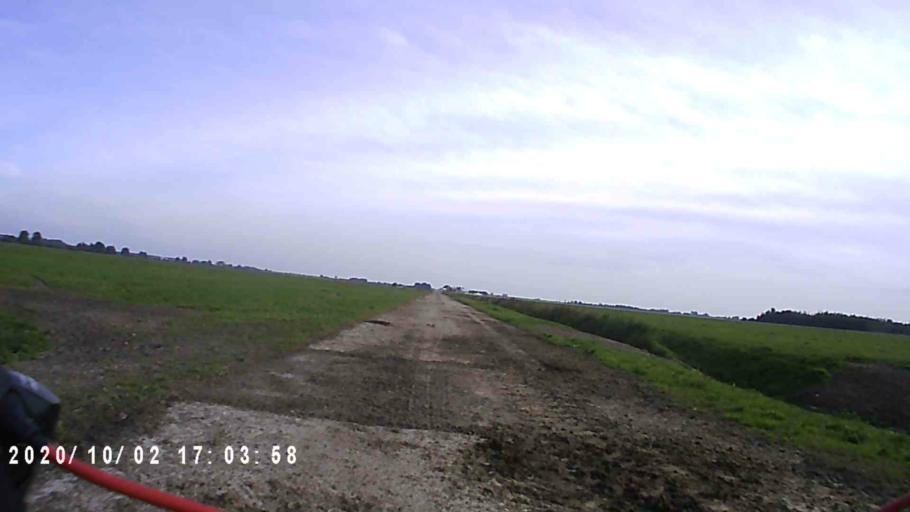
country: NL
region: Groningen
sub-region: Gemeente De Marne
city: Ulrum
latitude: 53.3404
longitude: 6.2661
